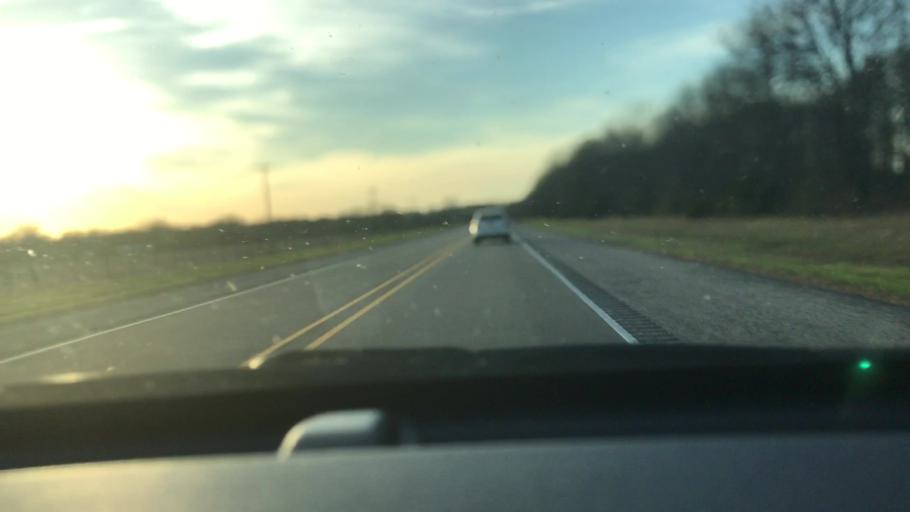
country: US
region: Texas
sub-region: Red River County
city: Clarksville
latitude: 33.5990
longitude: -94.9735
